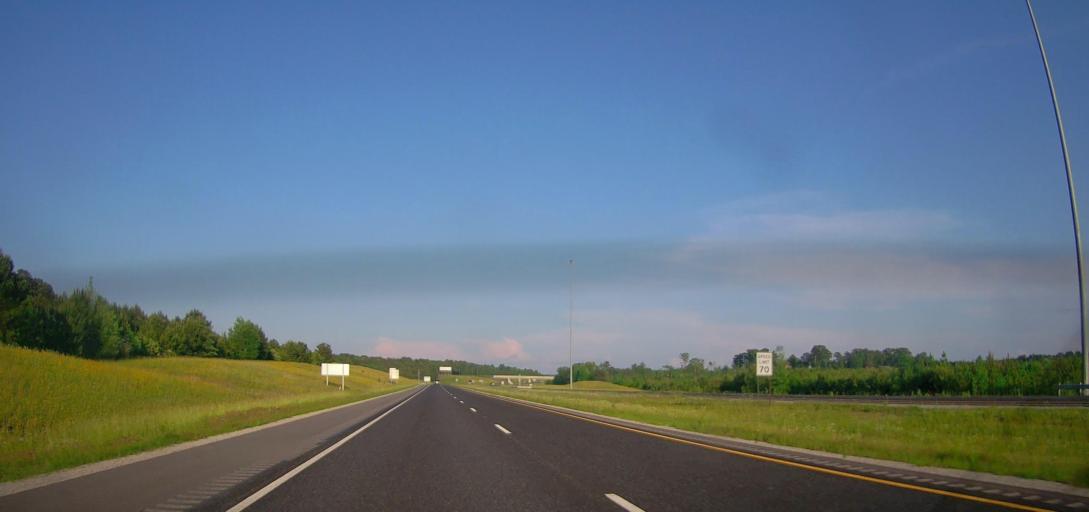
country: US
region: Alabama
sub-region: Marion County
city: Winfield
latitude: 33.9886
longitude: -87.7713
